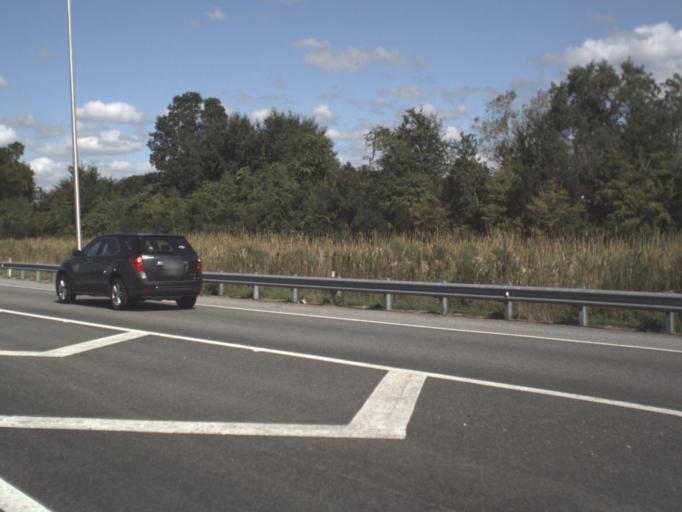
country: US
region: Florida
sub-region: Osceola County
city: Saint Cloud
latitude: 28.2237
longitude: -81.3195
